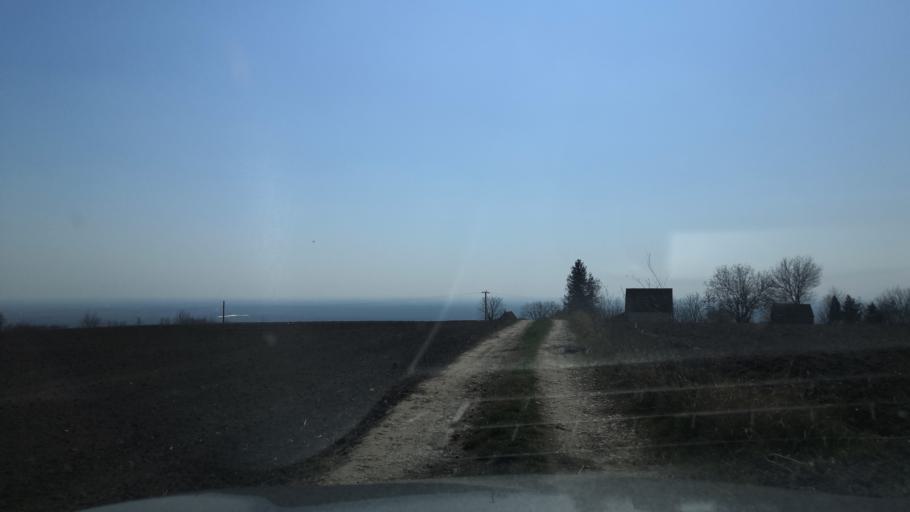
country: RS
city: Lok
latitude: 45.1631
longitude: 20.1866
